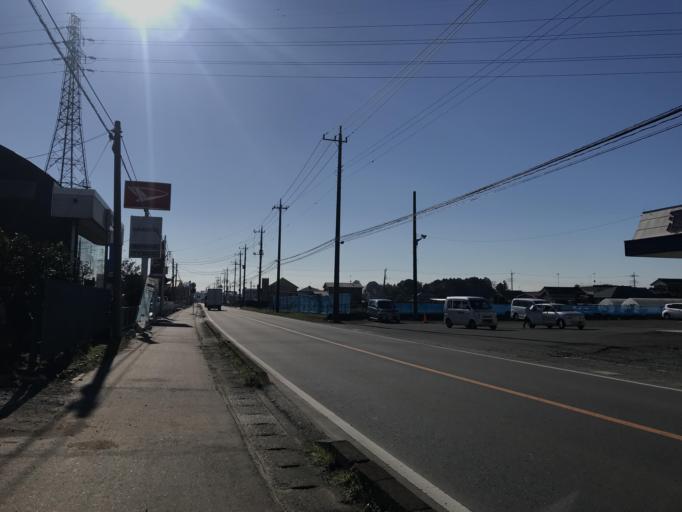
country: JP
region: Ibaraki
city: Sakai
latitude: 36.1648
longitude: 139.8095
